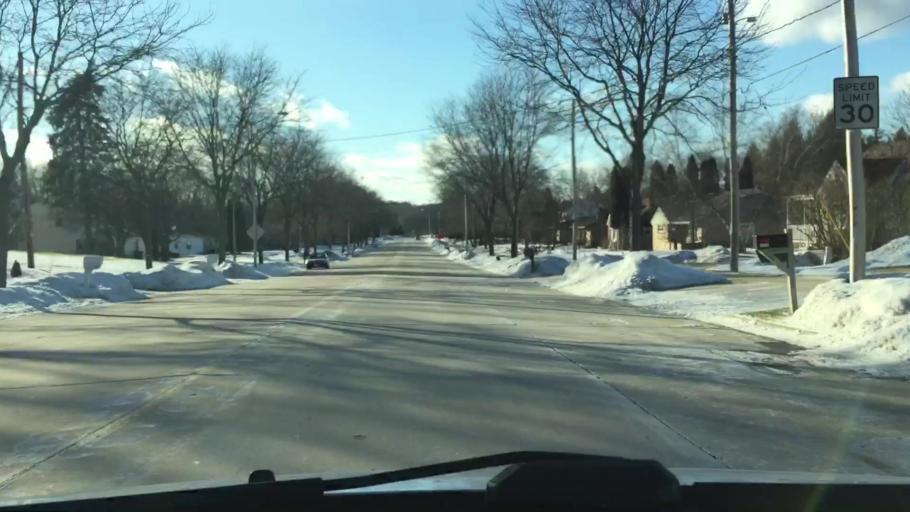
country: US
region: Wisconsin
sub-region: Milwaukee County
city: Greenfield
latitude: 42.9736
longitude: -88.0431
